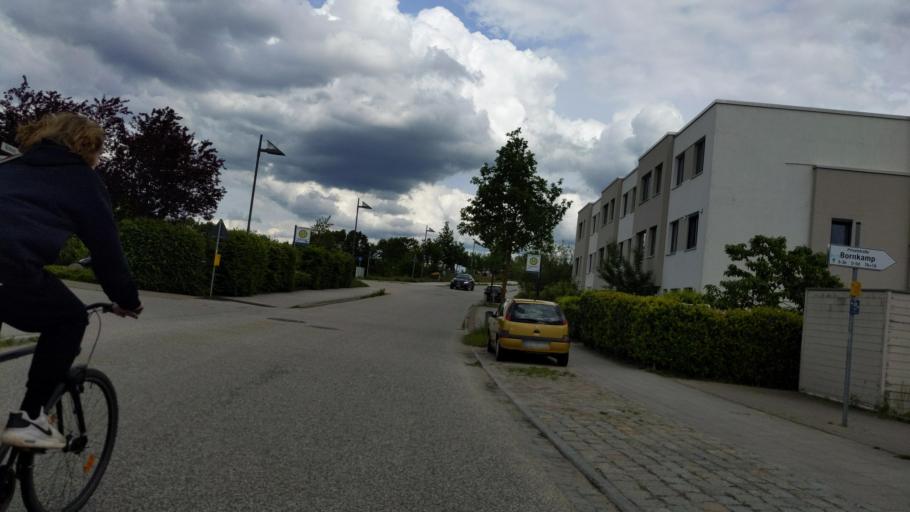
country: DE
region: Schleswig-Holstein
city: Luebeck
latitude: 53.8288
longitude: 10.6863
